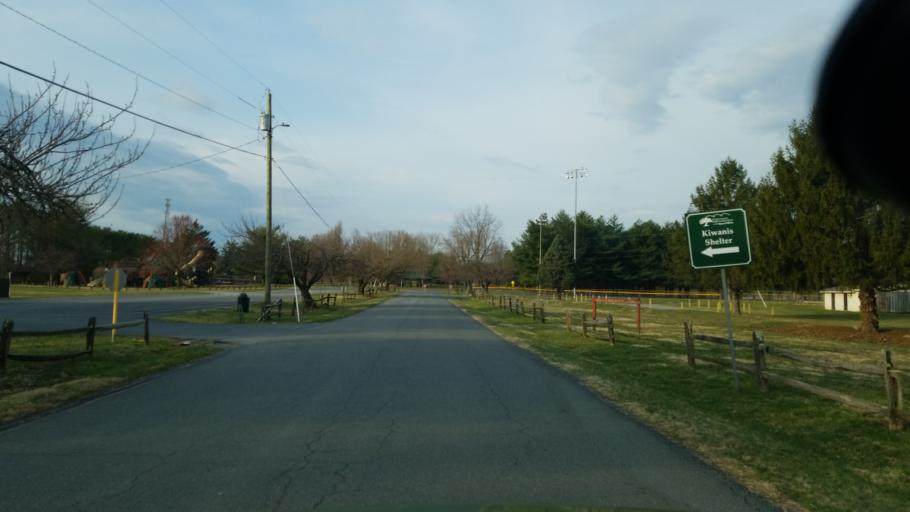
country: US
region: Virginia
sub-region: Clarke County
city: Berryville
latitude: 39.1639
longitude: -78.0012
